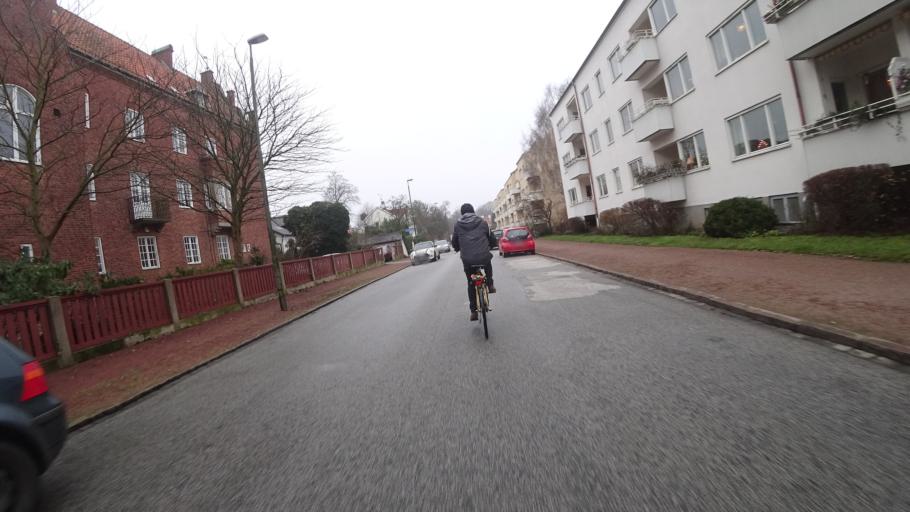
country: SE
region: Skane
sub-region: Malmo
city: Malmoe
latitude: 55.5959
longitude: 12.9714
